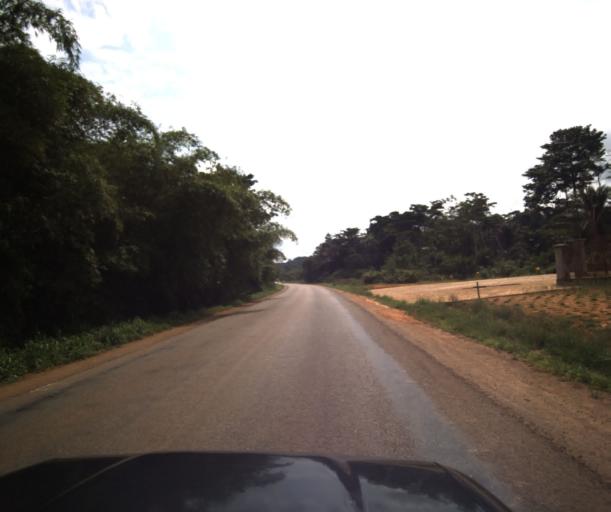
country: CM
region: Centre
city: Eseka
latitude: 3.8561
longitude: 10.5386
